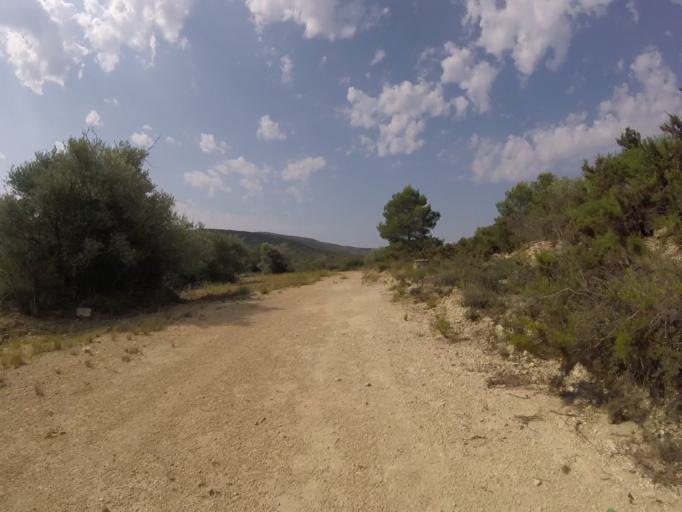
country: ES
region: Valencia
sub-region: Provincia de Castello
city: Alcala de Xivert
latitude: 40.3377
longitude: 0.1965
